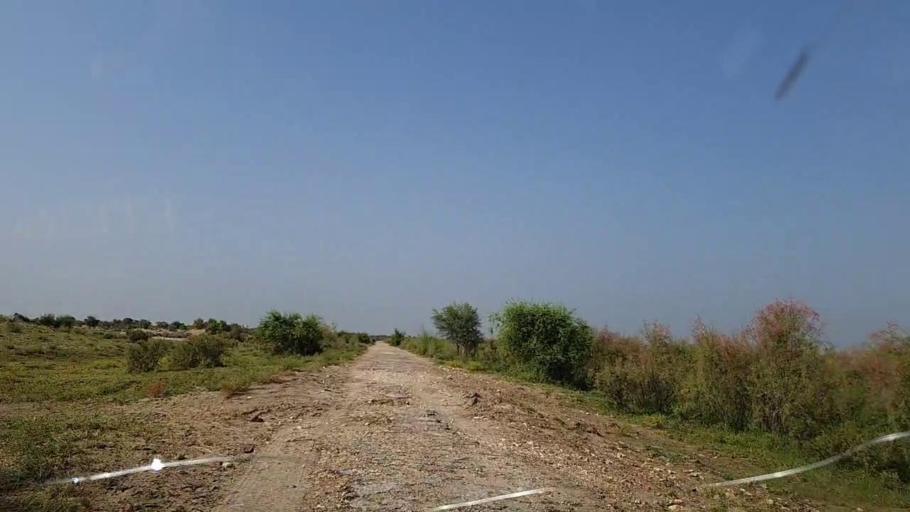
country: PK
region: Sindh
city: Khanpur
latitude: 27.6988
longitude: 69.3851
